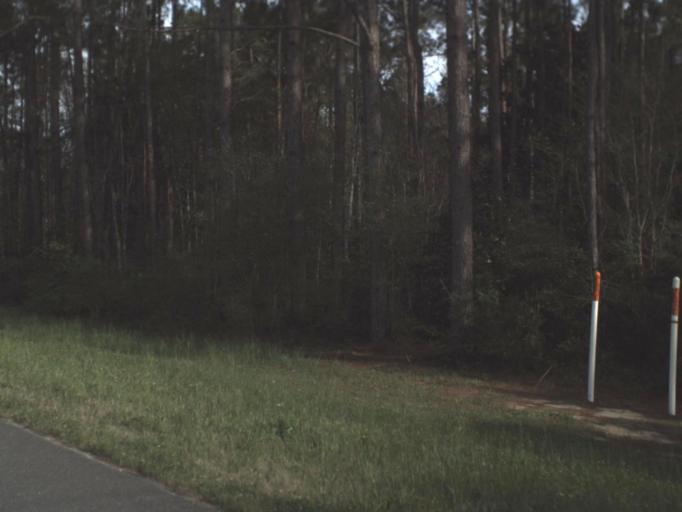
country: US
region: Florida
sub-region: Holmes County
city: Bonifay
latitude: 30.7795
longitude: -85.6362
